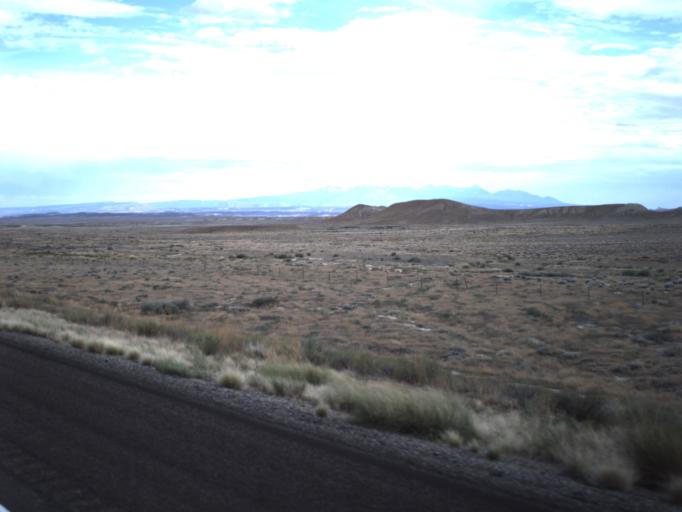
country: US
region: Utah
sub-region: Grand County
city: Moab
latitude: 38.9474
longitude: -109.6643
